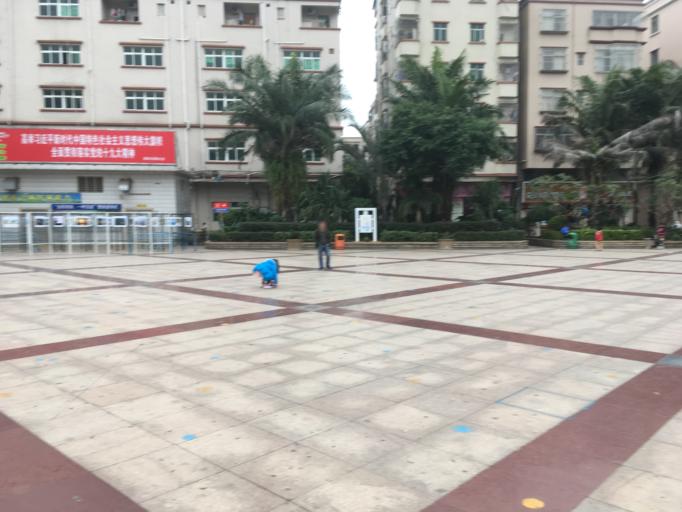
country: CN
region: Guangdong
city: Chang'an
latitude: 22.7952
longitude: 113.7386
